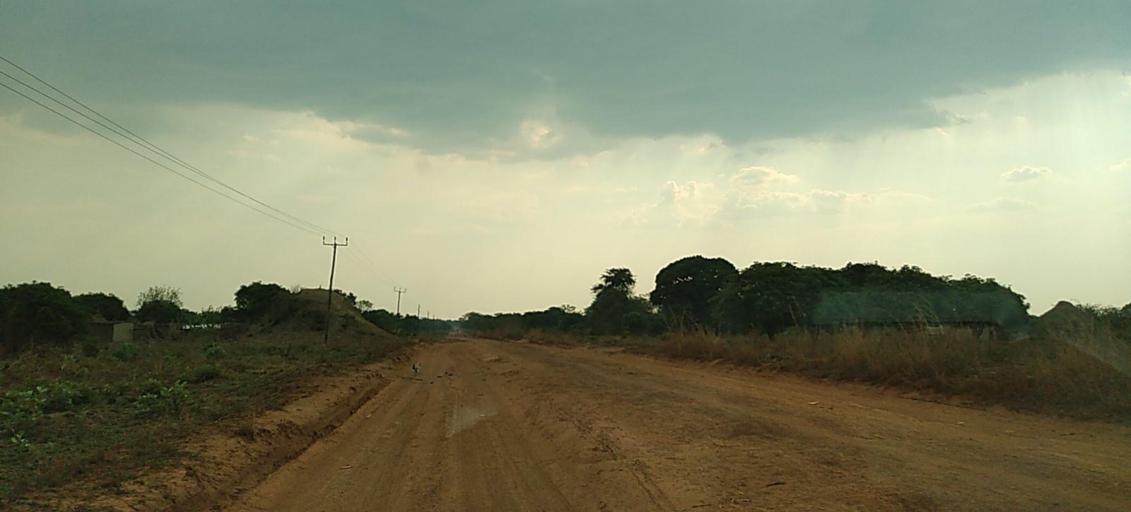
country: ZM
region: Copperbelt
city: Kalulushi
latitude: -12.9475
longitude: 27.9142
